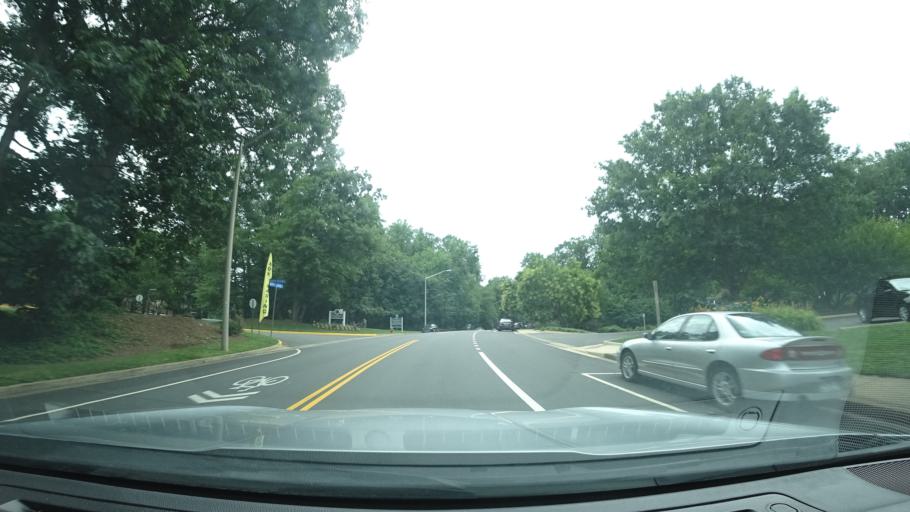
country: US
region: Virginia
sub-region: Fairfax County
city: Reston
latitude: 38.9698
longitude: -77.3376
